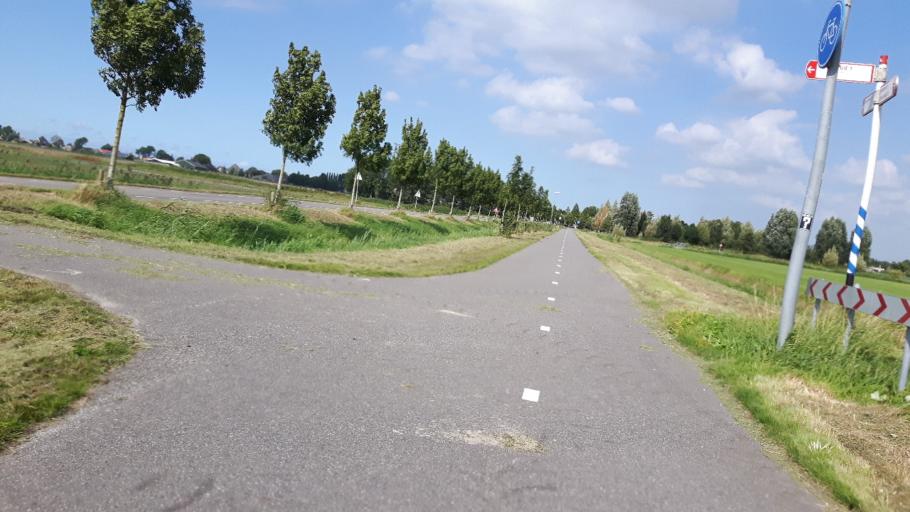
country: NL
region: North Holland
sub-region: Gemeente Medemblik
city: Opperdoes
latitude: 52.7176
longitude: 5.0915
